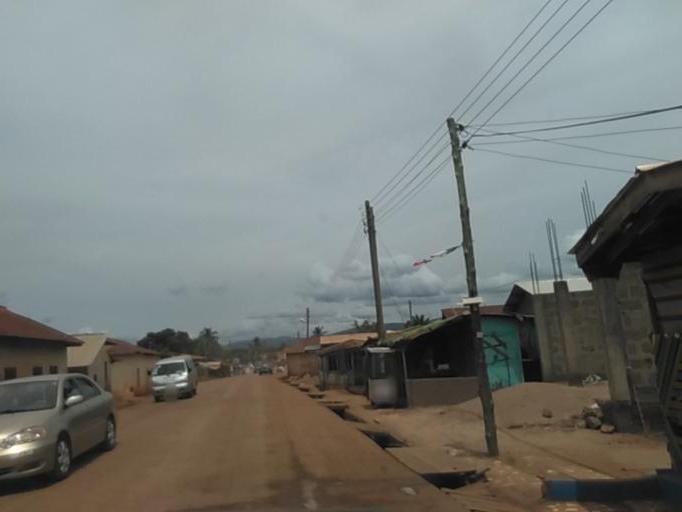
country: GH
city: Akropong
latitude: 6.1361
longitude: 0.0046
